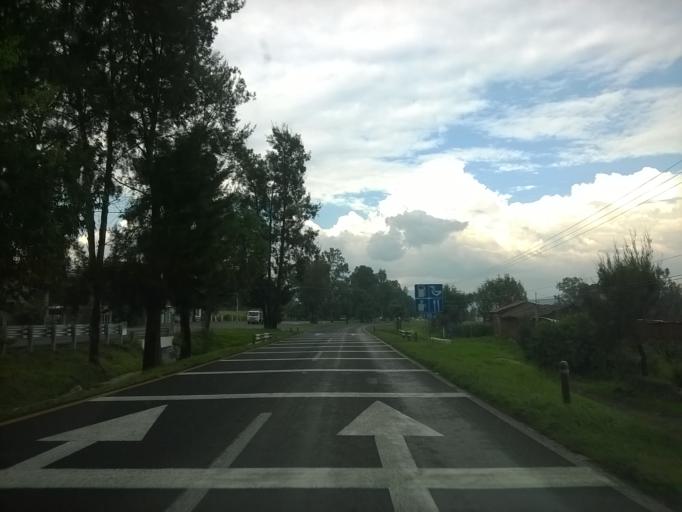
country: MX
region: Michoacan
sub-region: Huiramba
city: El Pedregal
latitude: 19.5327
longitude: -101.4749
